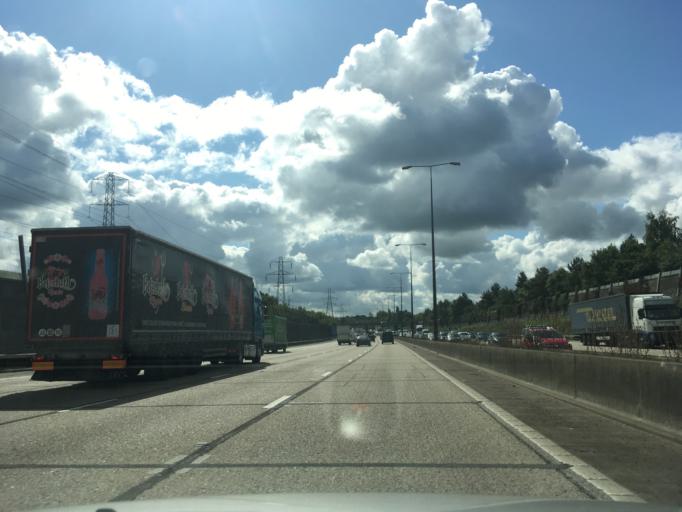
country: GB
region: England
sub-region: Surrey
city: Byfleet
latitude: 51.3438
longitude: -0.4853
